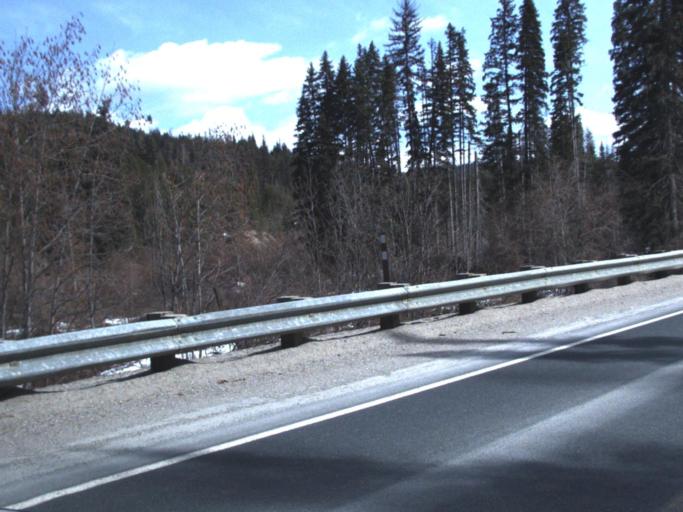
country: US
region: Washington
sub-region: Stevens County
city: Chewelah
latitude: 48.5395
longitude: -117.6015
